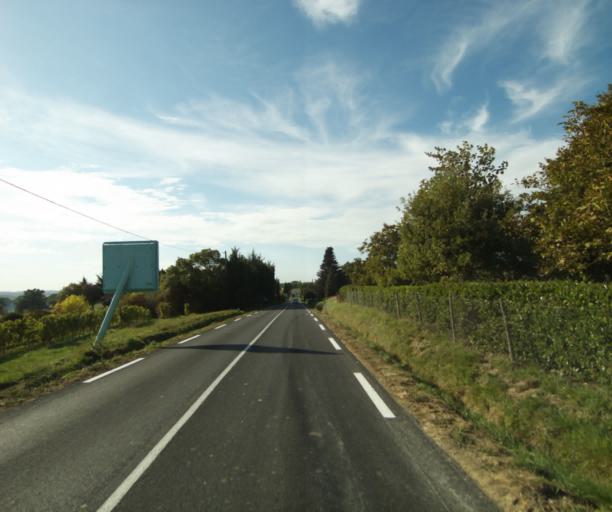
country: FR
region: Midi-Pyrenees
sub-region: Departement du Gers
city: Eauze
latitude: 43.8574
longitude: 0.0686
